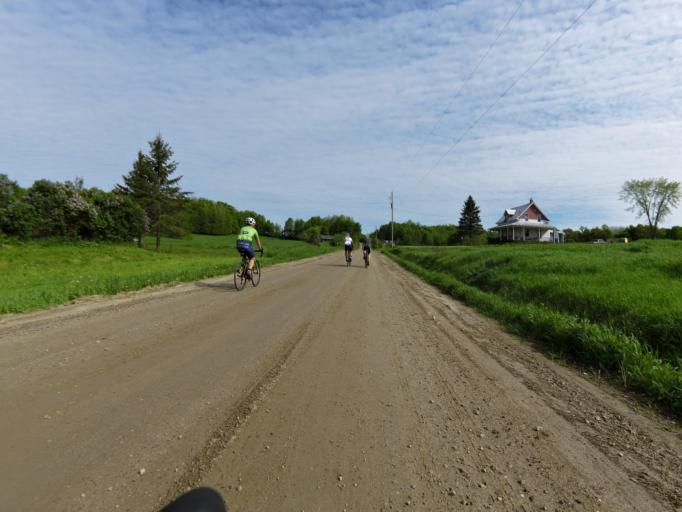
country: CA
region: Quebec
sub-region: Outaouais
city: Wakefield
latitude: 45.6990
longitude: -75.8956
